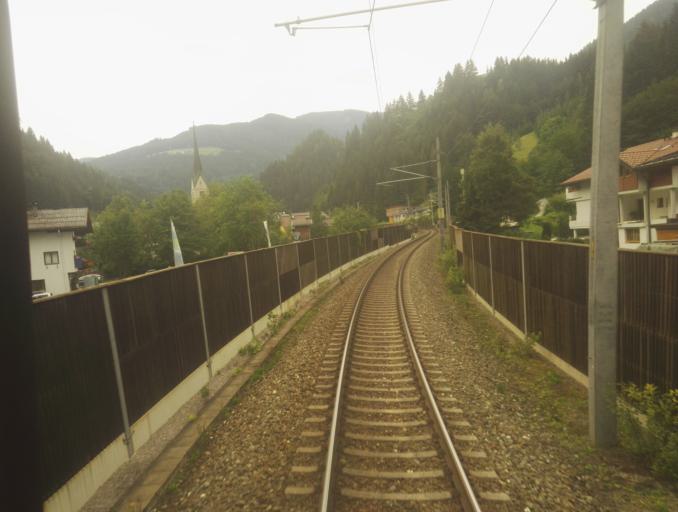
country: AT
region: Salzburg
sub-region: Politischer Bezirk Sankt Johann im Pongau
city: Huttau
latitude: 47.4175
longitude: 13.3048
